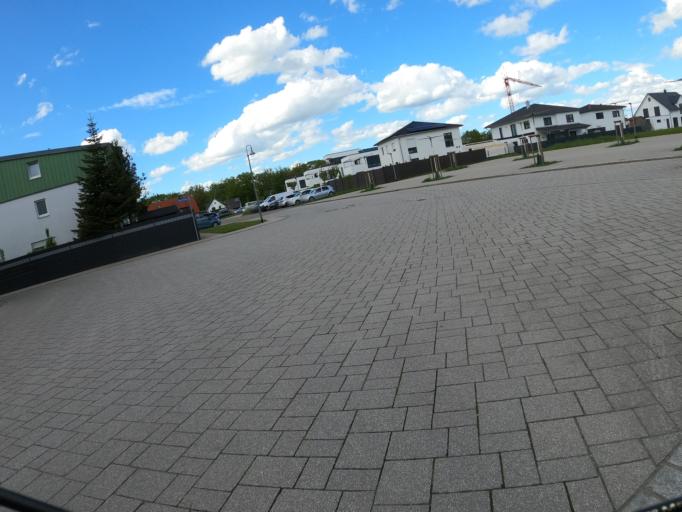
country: DE
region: Bavaria
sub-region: Swabia
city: Leipheim
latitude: 48.4509
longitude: 10.2336
